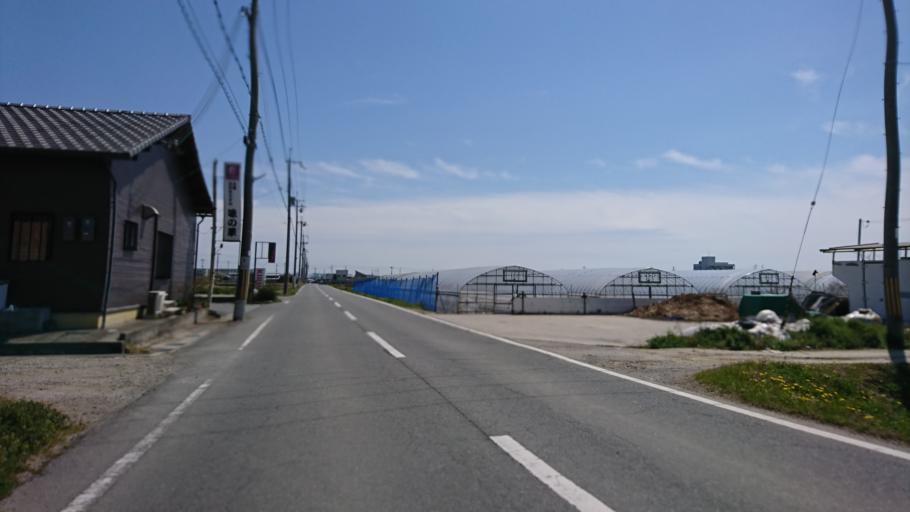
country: JP
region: Hyogo
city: Kakogawacho-honmachi
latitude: 34.7477
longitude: 134.8887
